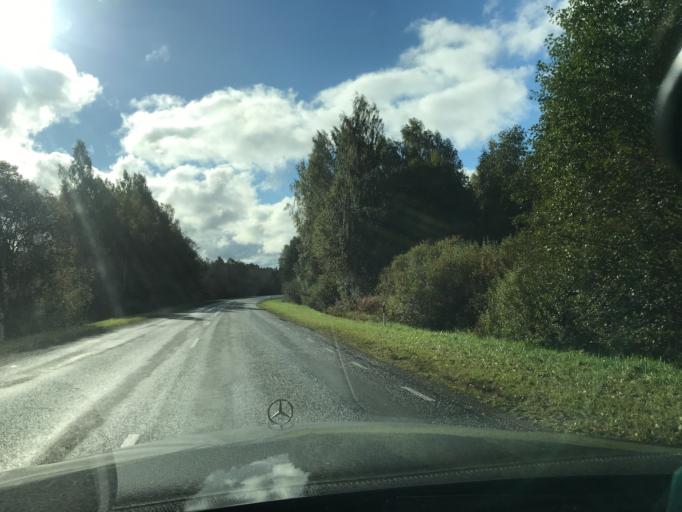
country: EE
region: Tartu
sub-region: Elva linn
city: Elva
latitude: 58.0017
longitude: 26.2679
